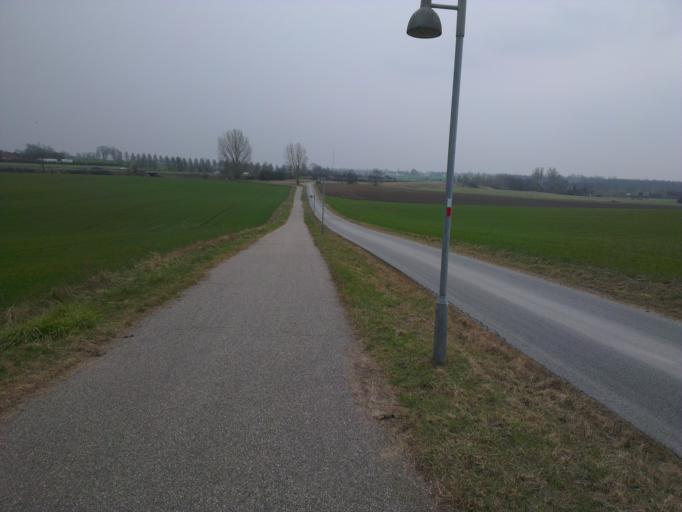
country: DK
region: Capital Region
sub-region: Frederikssund Kommune
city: Frederikssund
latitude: 55.8179
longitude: 12.1006
